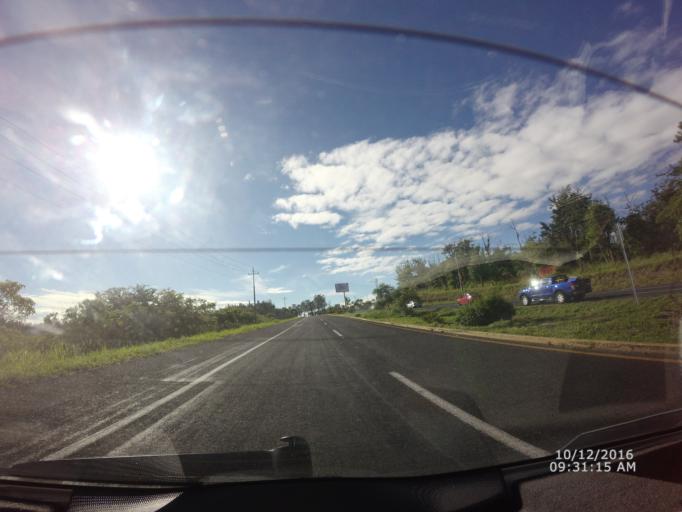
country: MX
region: Veracruz
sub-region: Emiliano Zapata
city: Jacarandas
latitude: 19.5021
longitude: -96.8438
